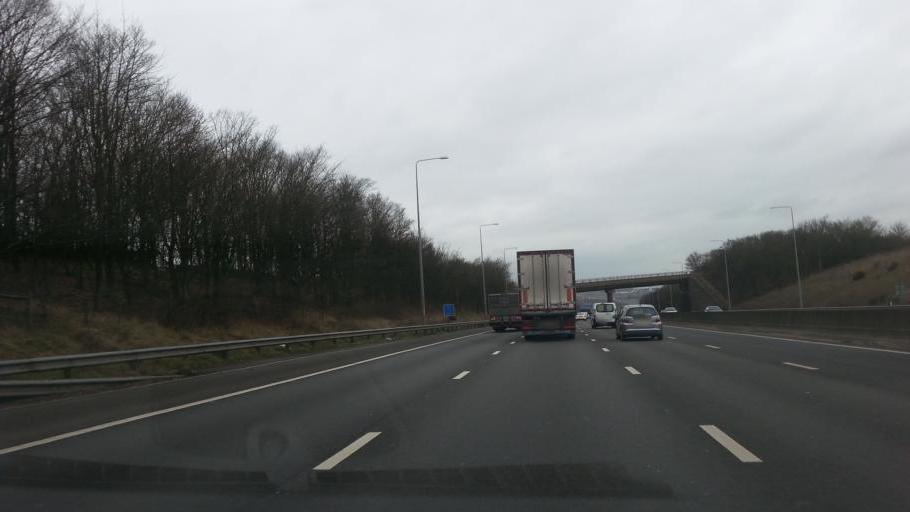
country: GB
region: England
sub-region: Derbyshire
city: Pinxton
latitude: 53.0793
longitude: -1.2936
